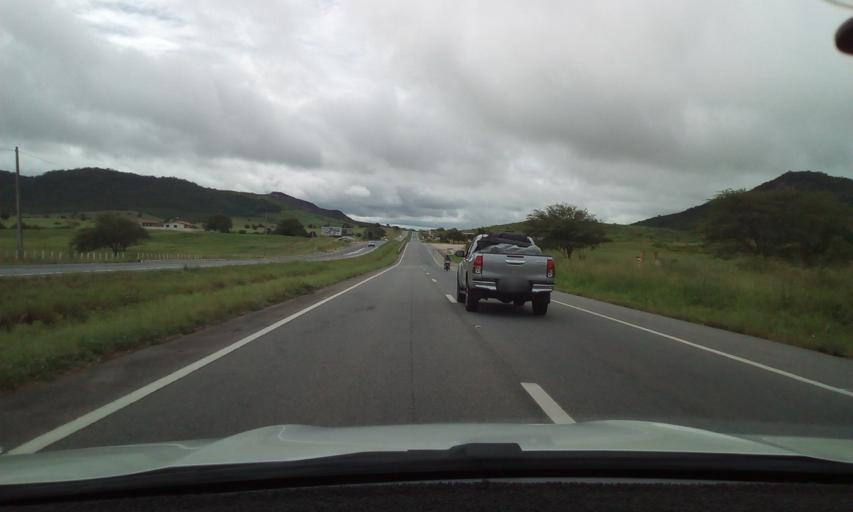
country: BR
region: Paraiba
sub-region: Gurinhem
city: Gurinhem
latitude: -7.1800
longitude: -35.4265
